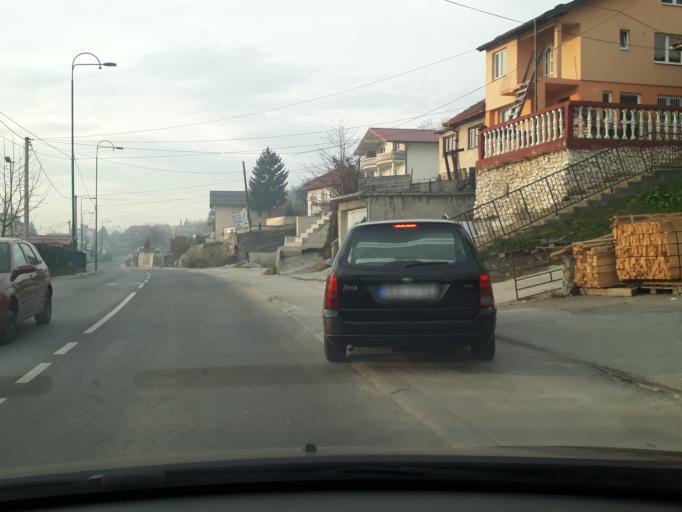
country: BA
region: Federation of Bosnia and Herzegovina
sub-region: Kanton Sarajevo
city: Sarajevo
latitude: 43.8534
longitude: 18.3318
